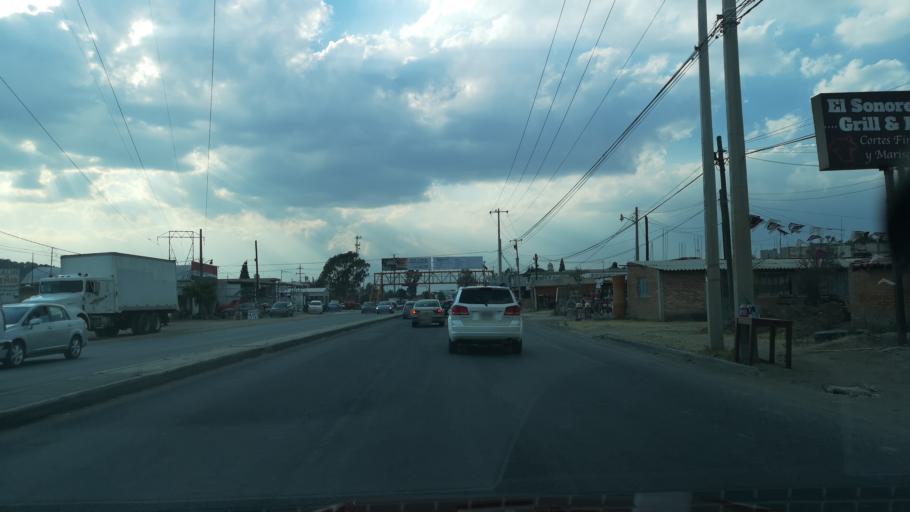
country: MX
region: Puebla
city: Cholula
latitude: 19.0775
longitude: -98.3236
